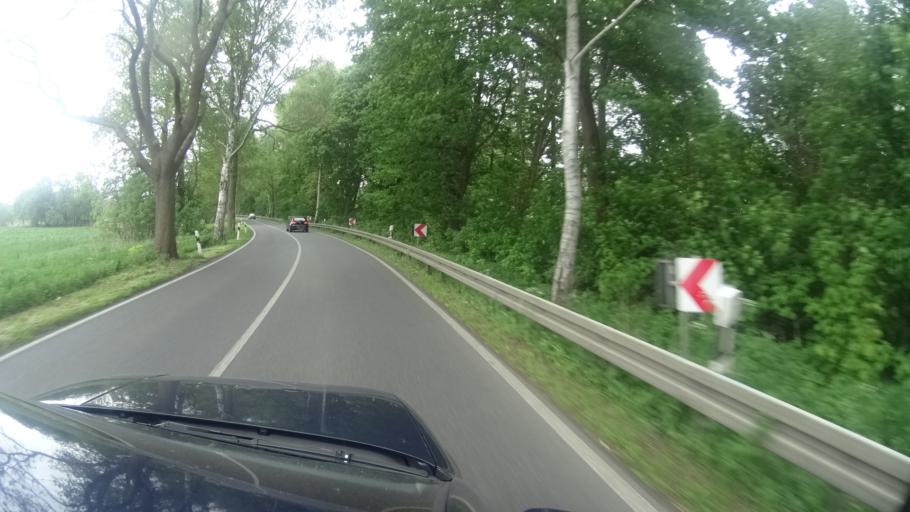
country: DE
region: Brandenburg
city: Fehrbellin
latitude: 52.8187
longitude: 12.7687
